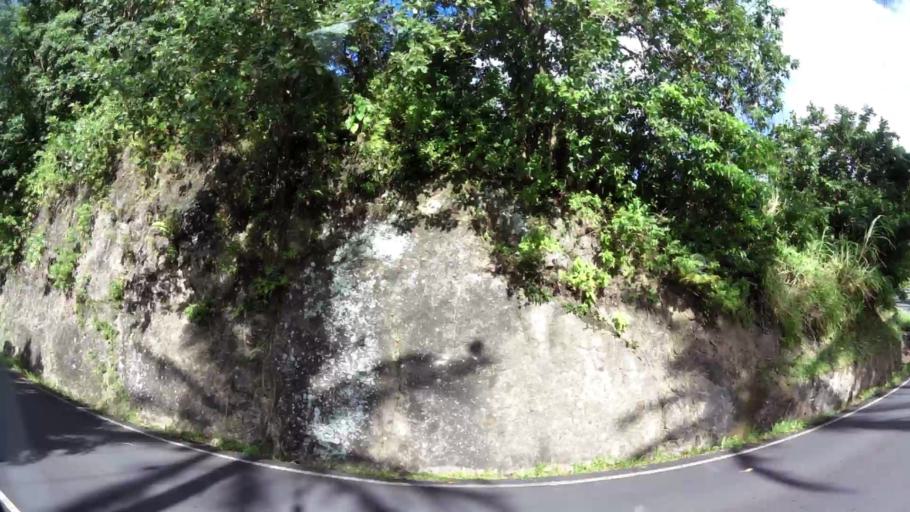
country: LC
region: Soufriere
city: Soufriere
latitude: 13.8671
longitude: -61.0499
